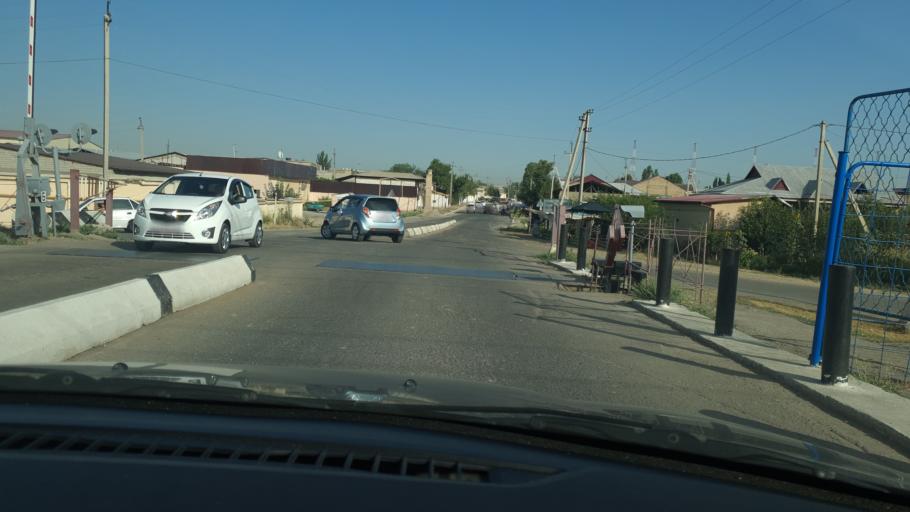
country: UZ
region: Toshkent
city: Urtaowul
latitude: 41.2012
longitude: 69.1555
